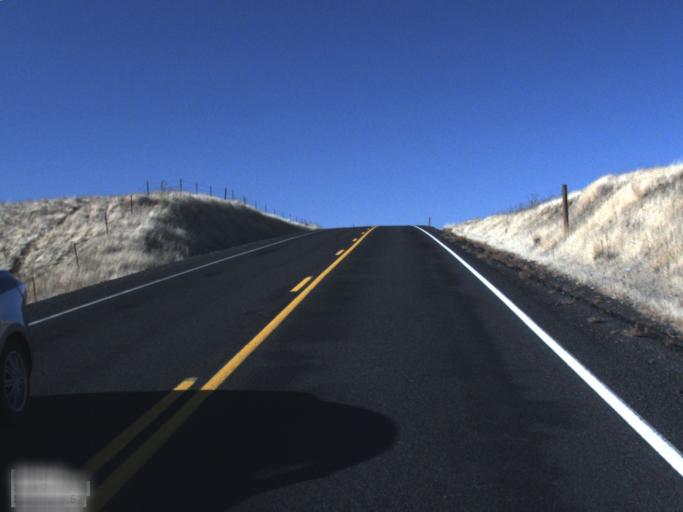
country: US
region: Washington
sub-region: Adams County
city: Ritzville
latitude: 46.7893
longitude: -118.2899
